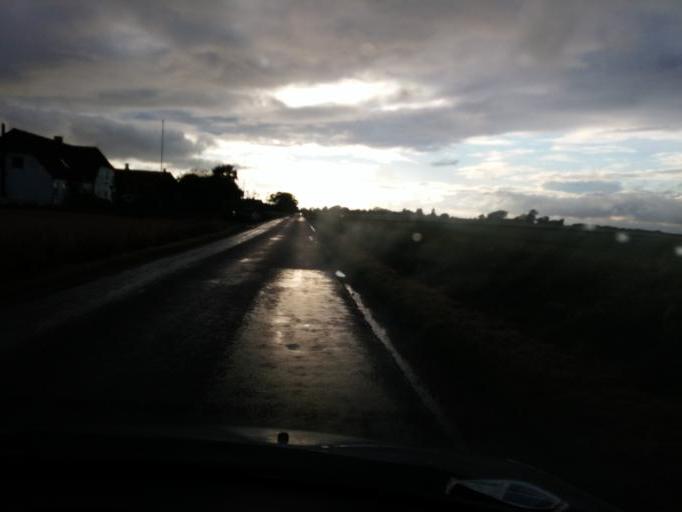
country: DK
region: South Denmark
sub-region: Kerteminde Kommune
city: Kerteminde
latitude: 55.5069
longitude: 10.6302
